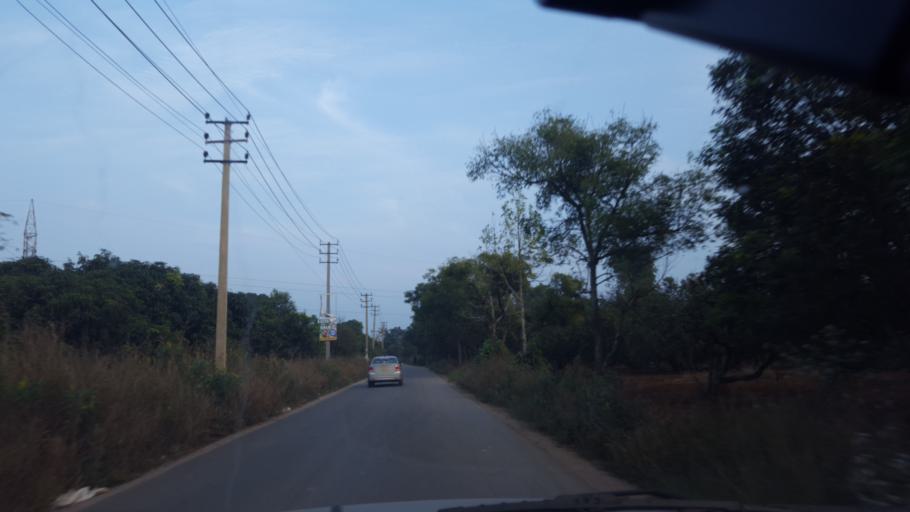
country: IN
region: Karnataka
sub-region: Bangalore Rural
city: Hoskote
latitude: 13.0773
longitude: 77.6976
